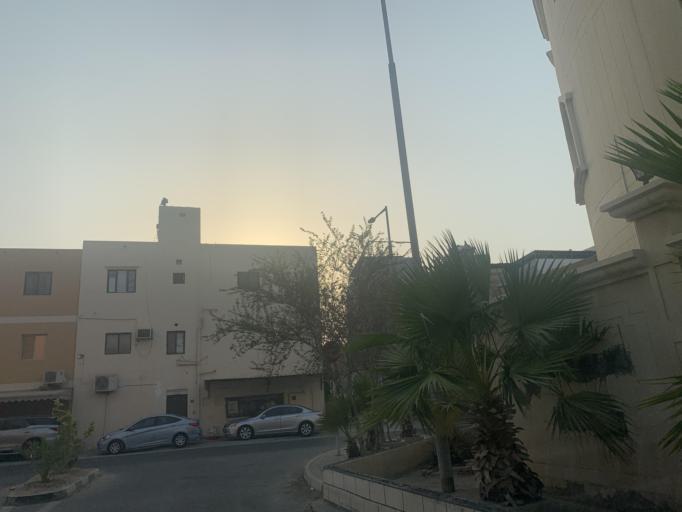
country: BH
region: Manama
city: Jidd Hafs
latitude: 26.2230
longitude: 50.5176
